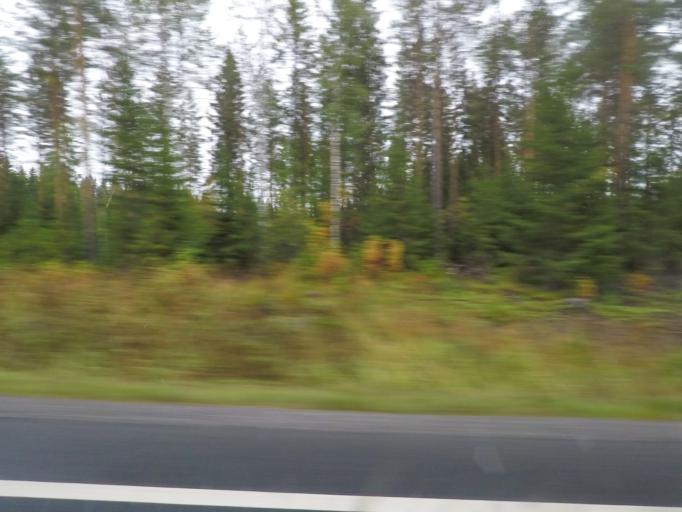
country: FI
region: Northern Savo
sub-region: Varkaus
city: Leppaevirta
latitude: 62.4997
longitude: 27.7440
